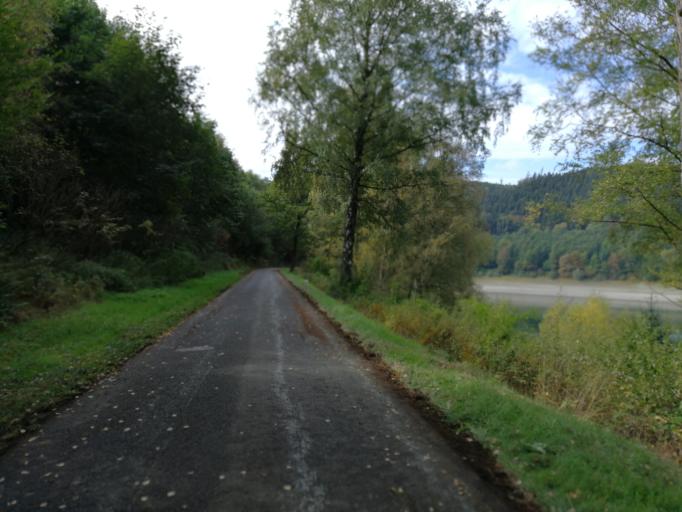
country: DE
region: North Rhine-Westphalia
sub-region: Regierungsbezirk Arnsberg
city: Meschede
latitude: 51.3262
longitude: 8.2647
